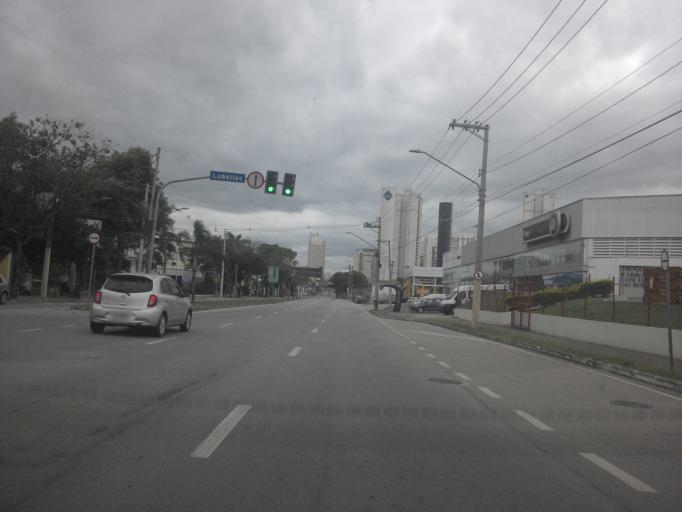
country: BR
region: Sao Paulo
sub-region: Sao Jose Dos Campos
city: Sao Jose dos Campos
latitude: -23.2299
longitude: -45.9126
